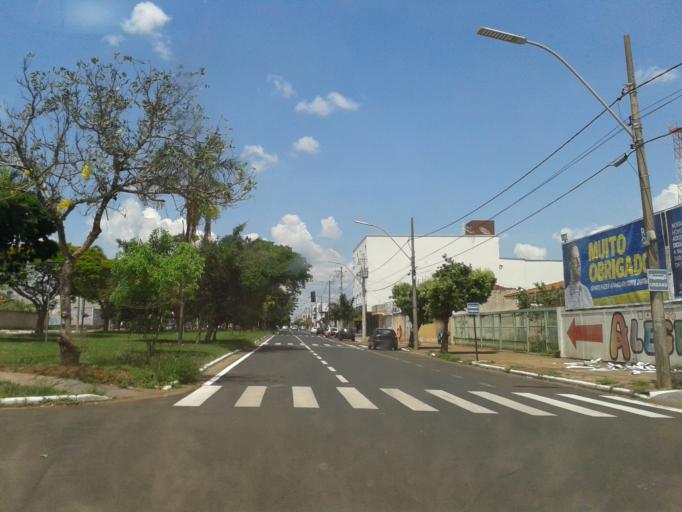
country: BR
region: Minas Gerais
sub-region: Araguari
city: Araguari
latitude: -18.6562
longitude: -48.1898
